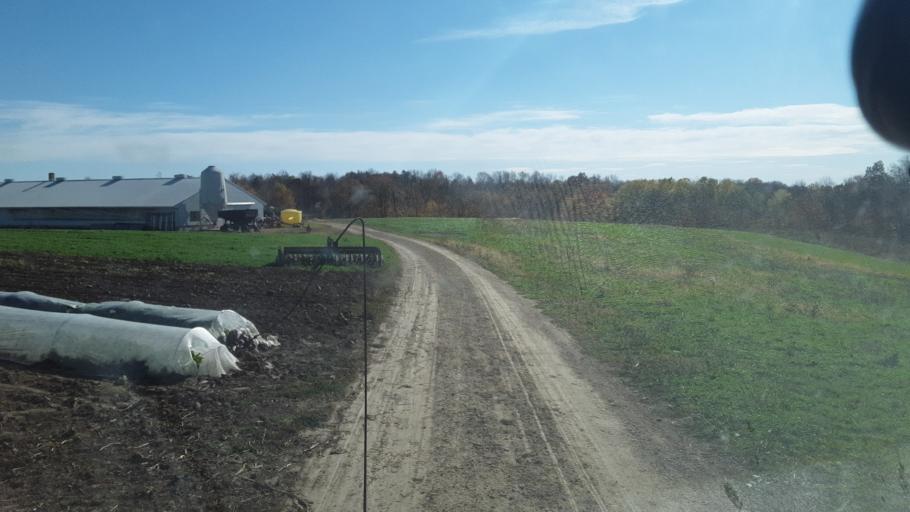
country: US
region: Wisconsin
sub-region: Vernon County
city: Hillsboro
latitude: 43.6844
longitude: -90.4097
